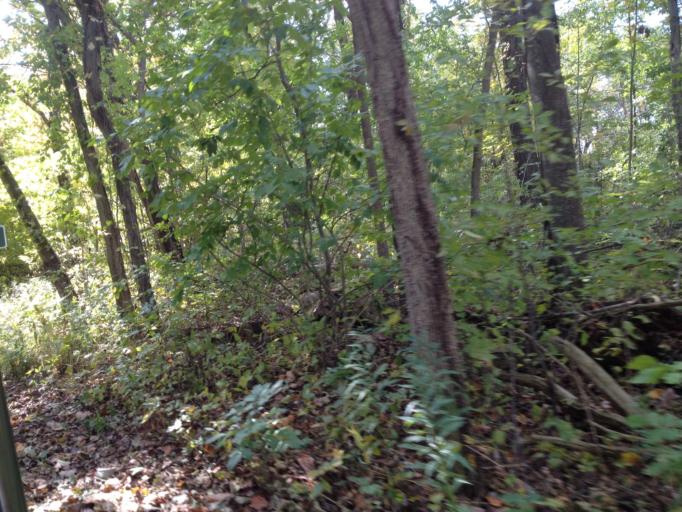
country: US
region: Ohio
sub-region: Erie County
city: Sandusky
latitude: 41.9312
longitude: -82.5144
